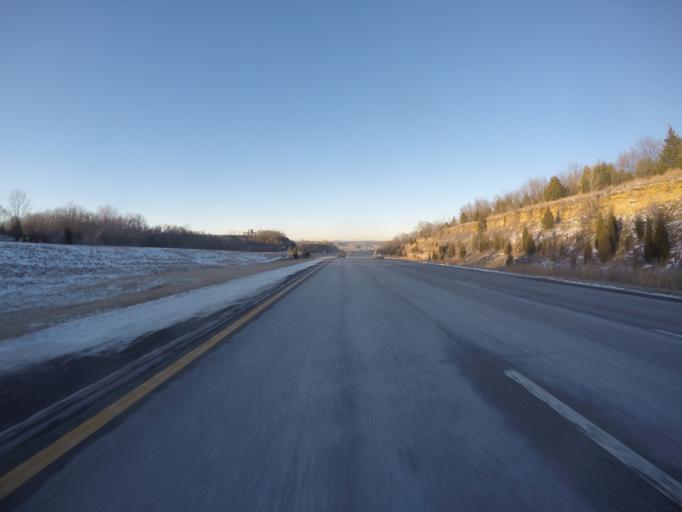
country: US
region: Kansas
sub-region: Wyandotte County
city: Edwardsville
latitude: 39.0349
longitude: -94.7879
